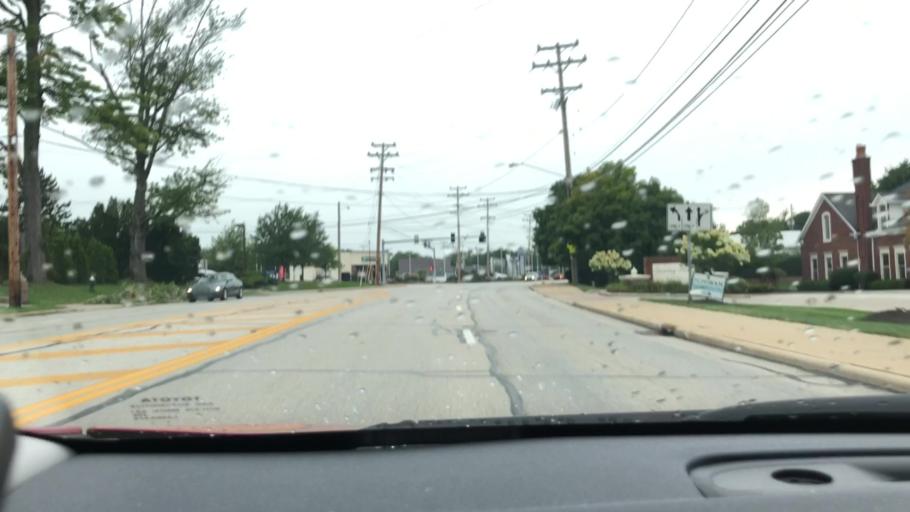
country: US
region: Ohio
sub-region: Cuyahoga County
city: Fairview Park
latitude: 41.4564
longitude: -81.8815
